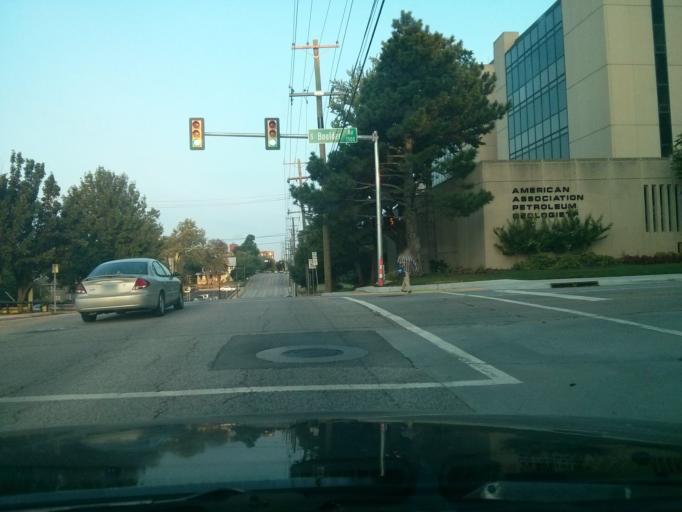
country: US
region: Oklahoma
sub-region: Tulsa County
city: Tulsa
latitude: 36.1406
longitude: -95.9883
